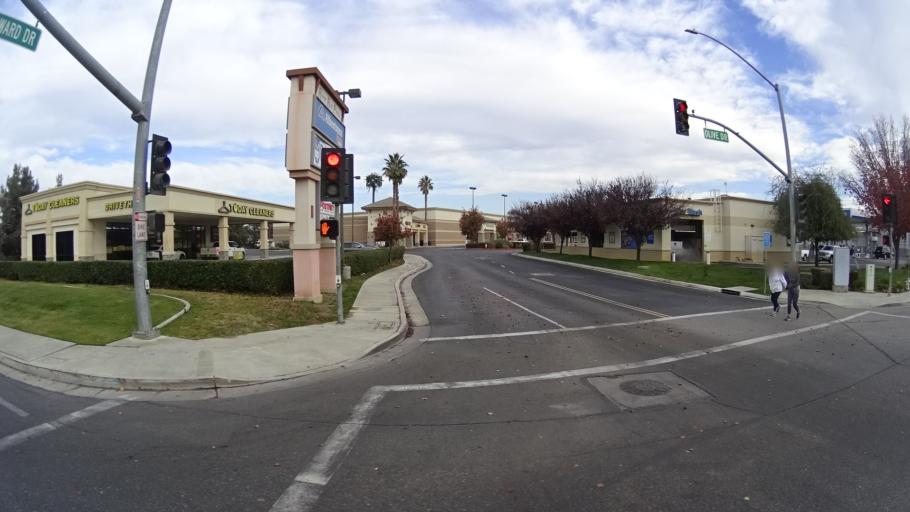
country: US
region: California
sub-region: Kern County
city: Greenacres
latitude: 35.4126
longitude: -119.0942
